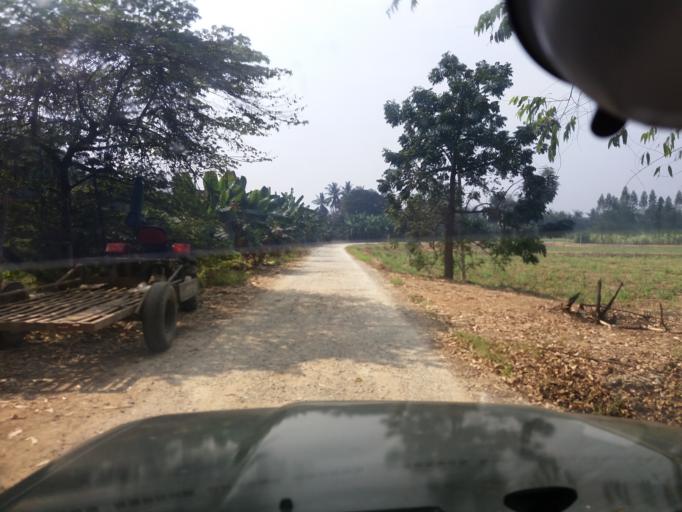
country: TH
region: Sing Buri
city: Bang Racham
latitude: 14.8992
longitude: 100.2162
